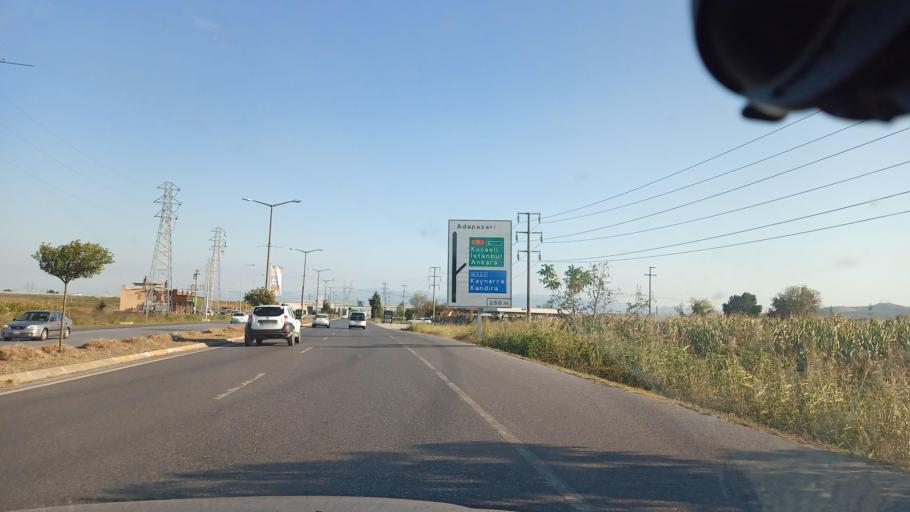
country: TR
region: Sakarya
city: Kazimpasa
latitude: 40.8315
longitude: 30.3479
